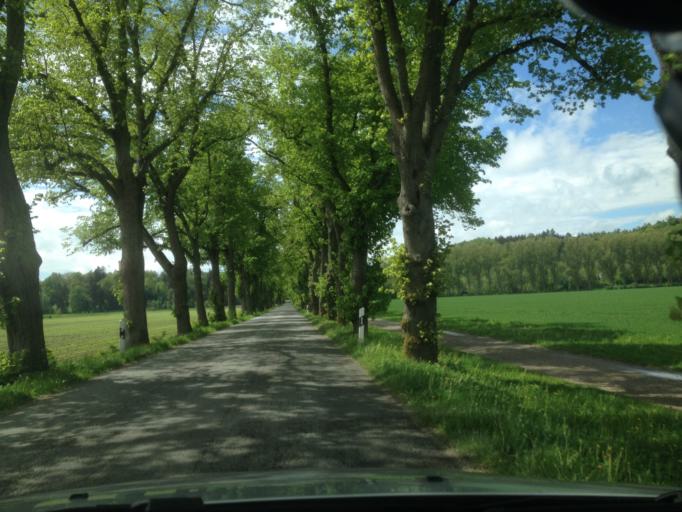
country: DE
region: Bavaria
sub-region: Swabia
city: Stadtbergen
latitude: 48.3359
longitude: 10.8378
